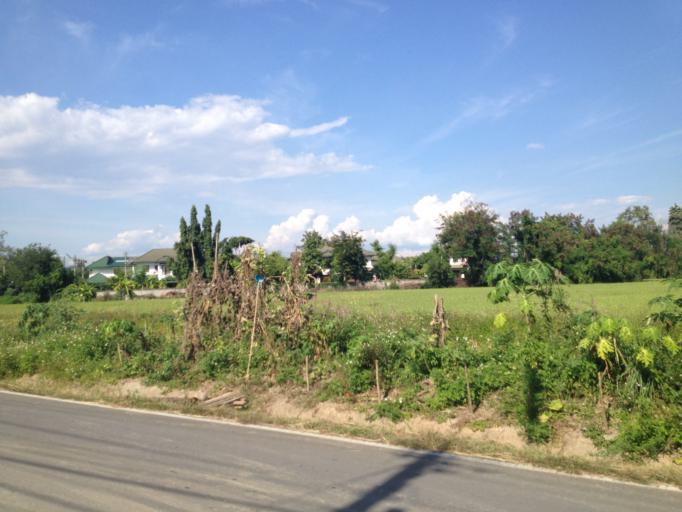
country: TH
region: Chiang Mai
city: Hang Dong
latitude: 18.7270
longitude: 98.9566
